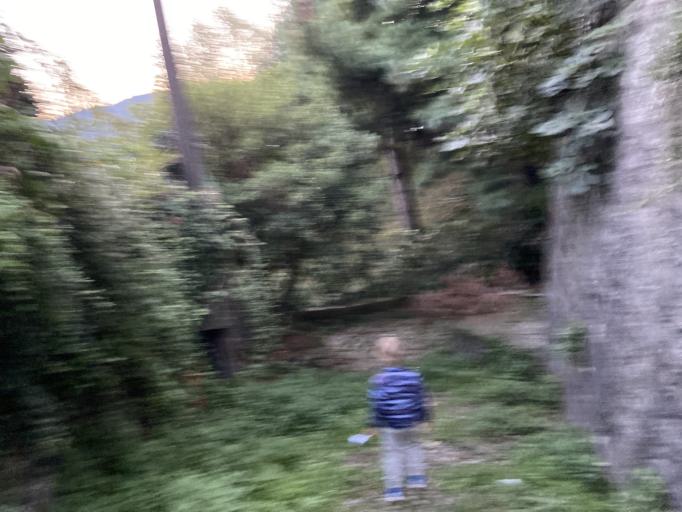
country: IT
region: Piedmont
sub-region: Provincia Verbano-Cusio-Ossola
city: Verbania
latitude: 45.9327
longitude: 8.5431
